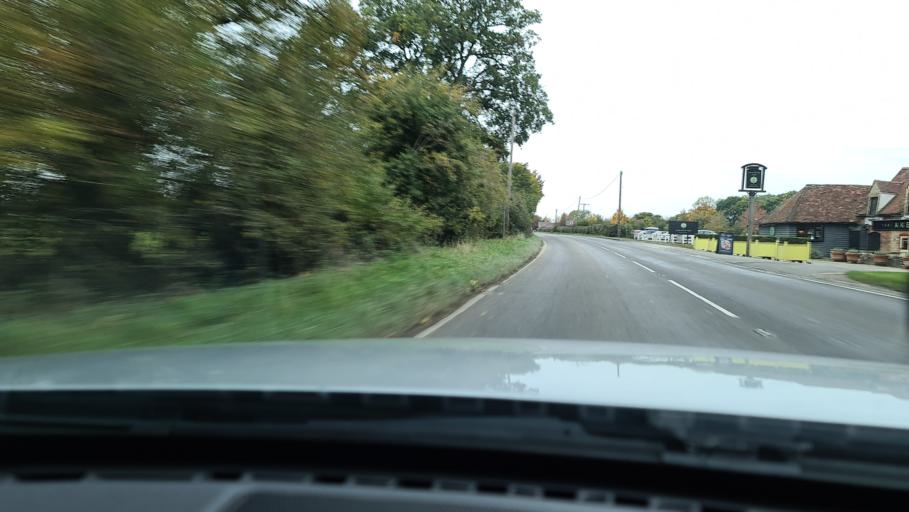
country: GB
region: England
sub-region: Buckinghamshire
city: Steeple Claydon
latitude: 51.8637
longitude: -0.9934
